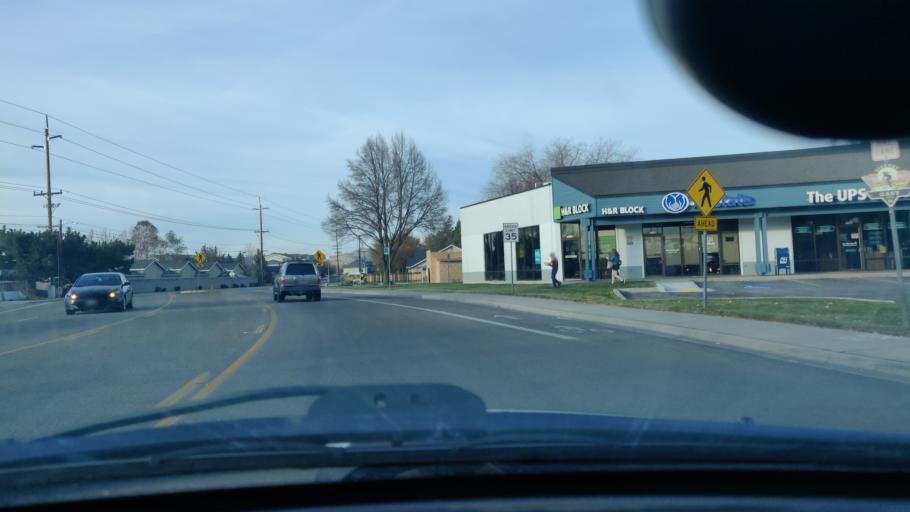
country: US
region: Idaho
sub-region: Ada County
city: Garden City
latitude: 43.6690
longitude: -116.2788
